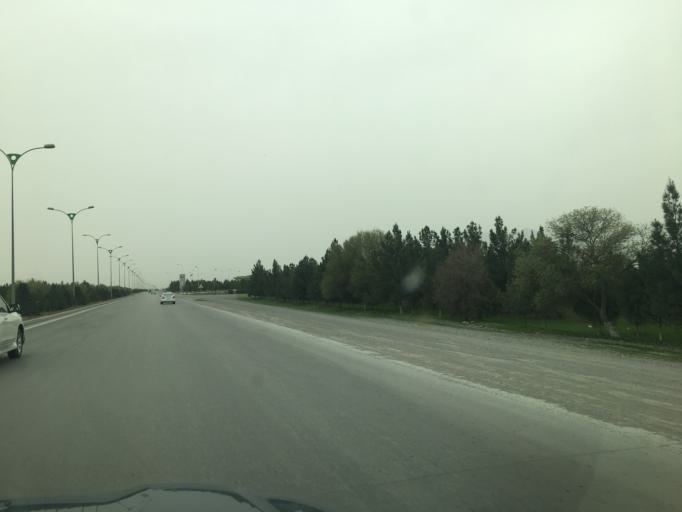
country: TM
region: Ahal
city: Abadan
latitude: 38.1463
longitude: 57.9894
